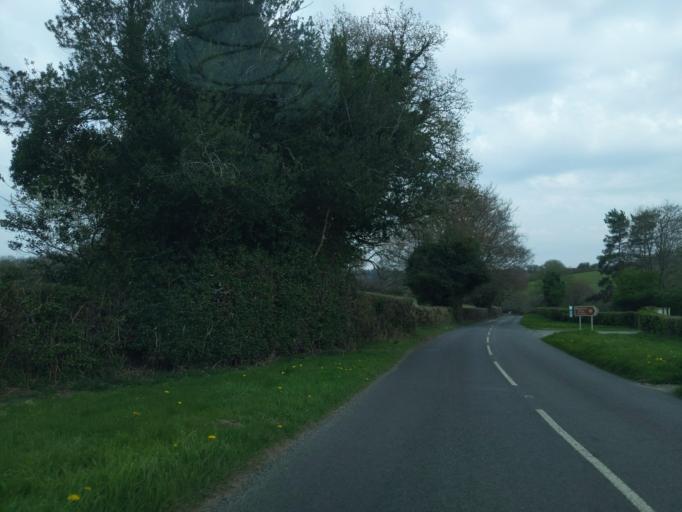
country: GB
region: England
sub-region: Devon
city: Ashburton
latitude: 50.6484
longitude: -3.8159
